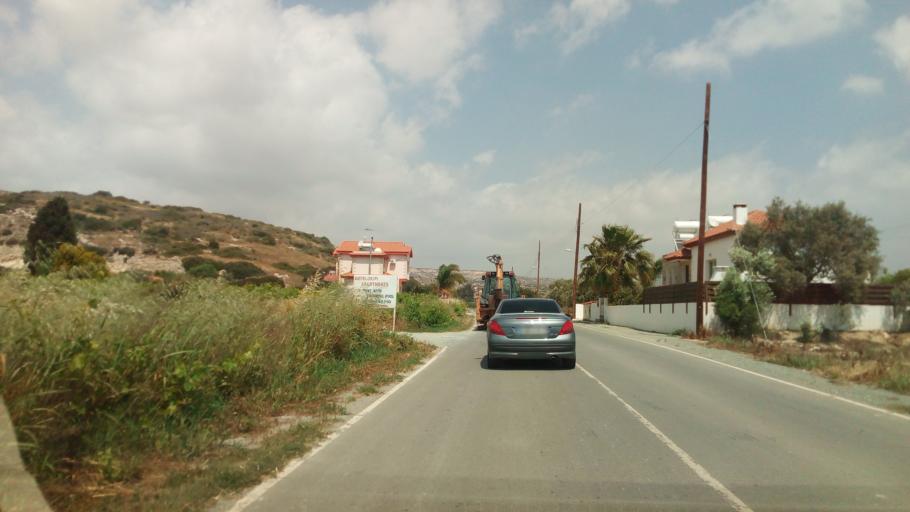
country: CY
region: Limassol
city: Pissouri
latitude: 34.6601
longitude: 32.7283
